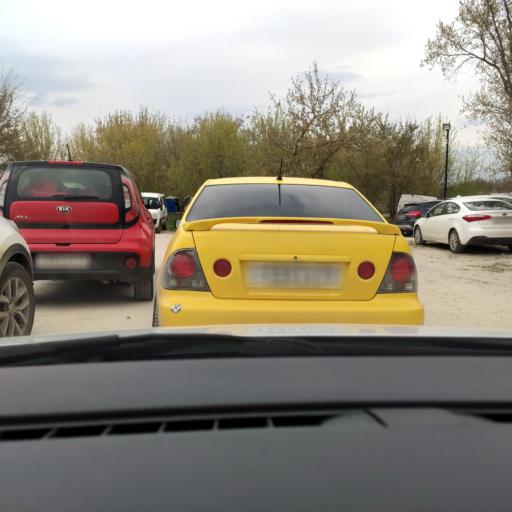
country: RU
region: Lipetsk
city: Donskoye
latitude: 52.6785
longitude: 38.9153
